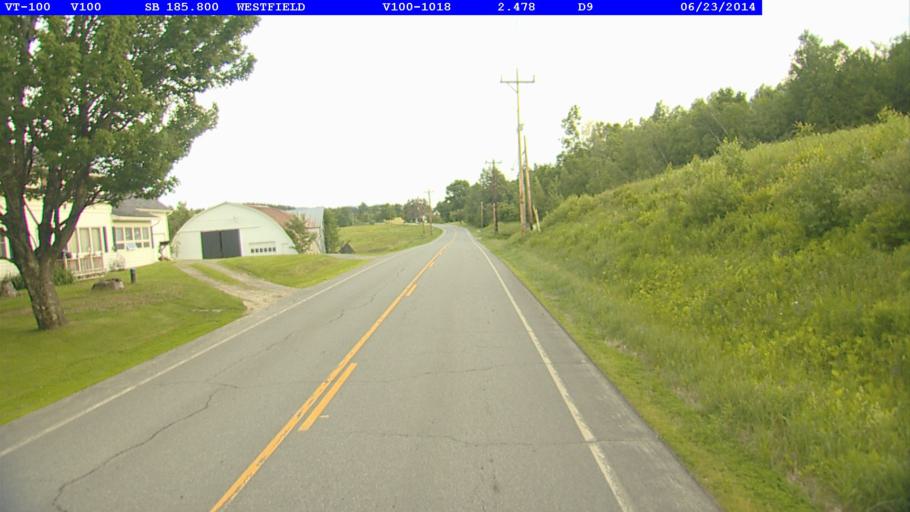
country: US
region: Vermont
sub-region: Orleans County
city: Newport
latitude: 44.8704
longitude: -72.4327
